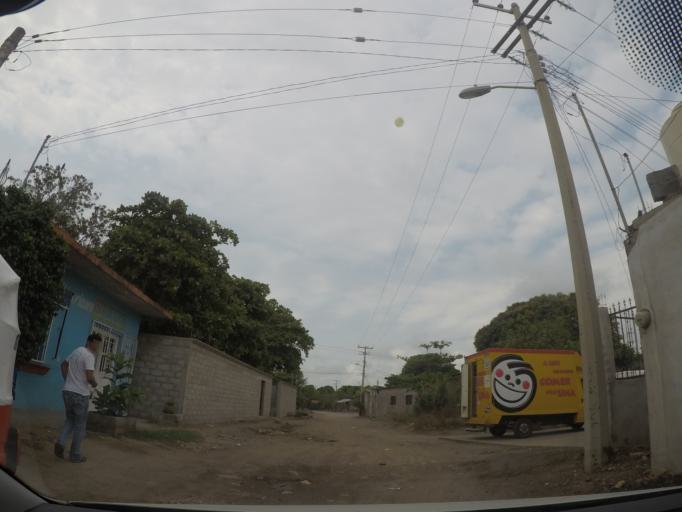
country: MX
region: Oaxaca
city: Juchitan de Zaragoza
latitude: 16.4524
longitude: -95.0146
